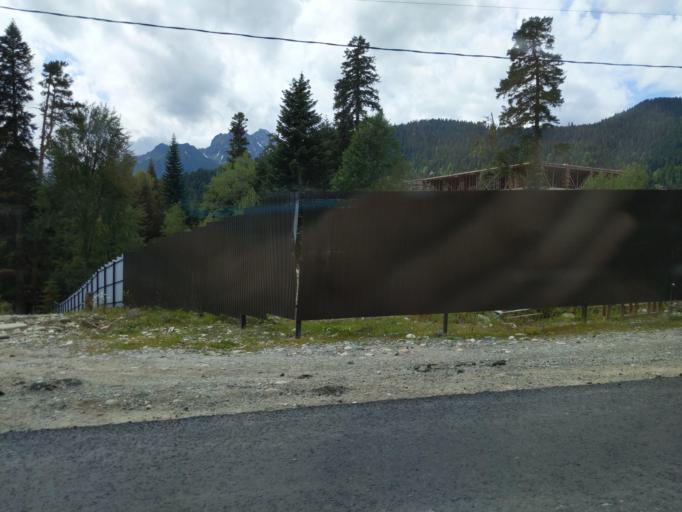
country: RU
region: Karachayevo-Cherkesiya
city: Nizhniy Arkhyz
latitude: 43.5374
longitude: 41.2114
